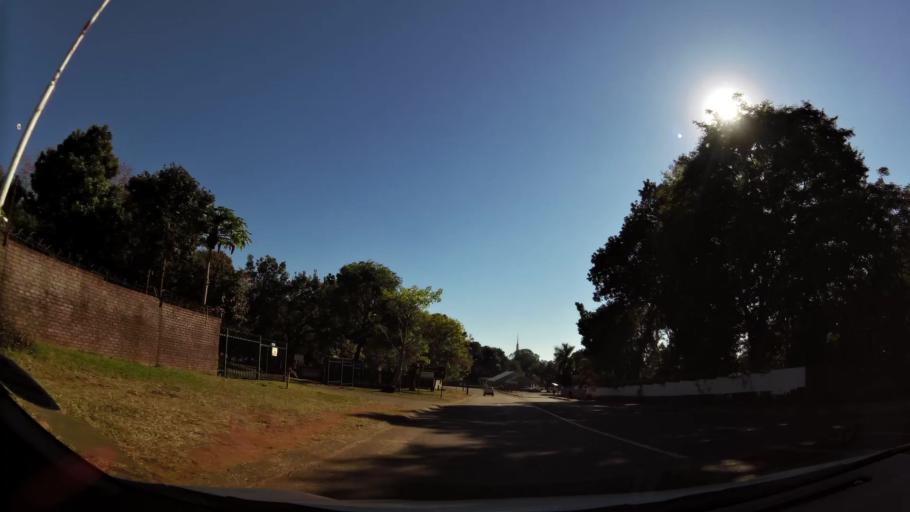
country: ZA
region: Limpopo
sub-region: Mopani District Municipality
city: Tzaneen
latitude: -23.8358
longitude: 30.1546
